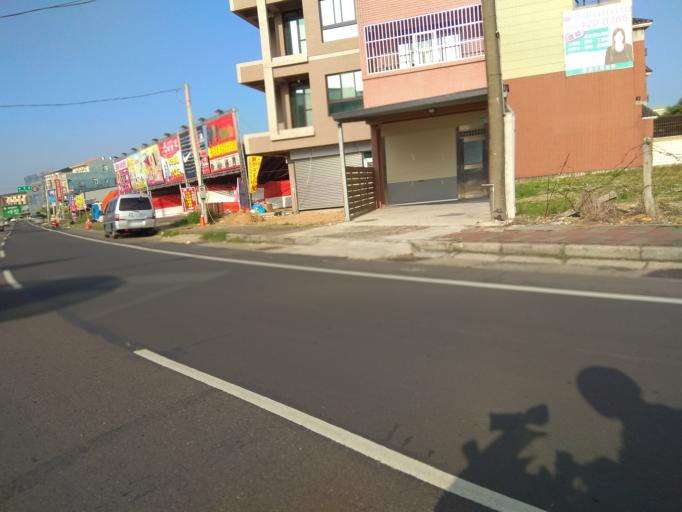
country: TW
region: Taiwan
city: Taoyuan City
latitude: 24.9642
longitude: 121.1502
